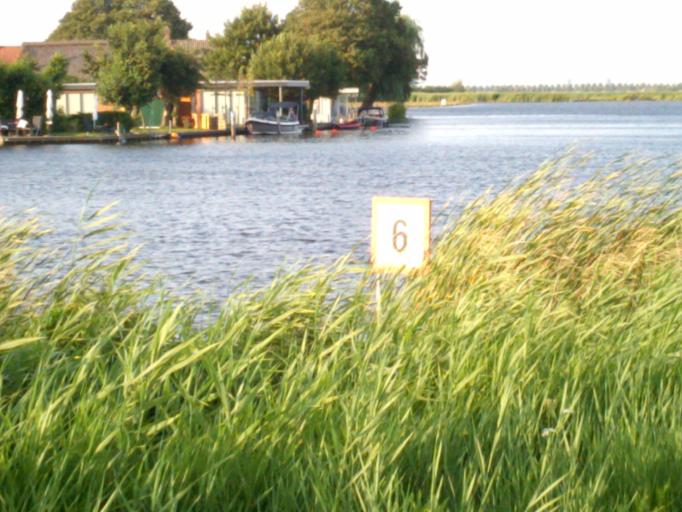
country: NL
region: South Holland
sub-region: Gemeente Kaag en Braassem
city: Oude Wetering
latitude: 52.2064
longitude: 4.5890
